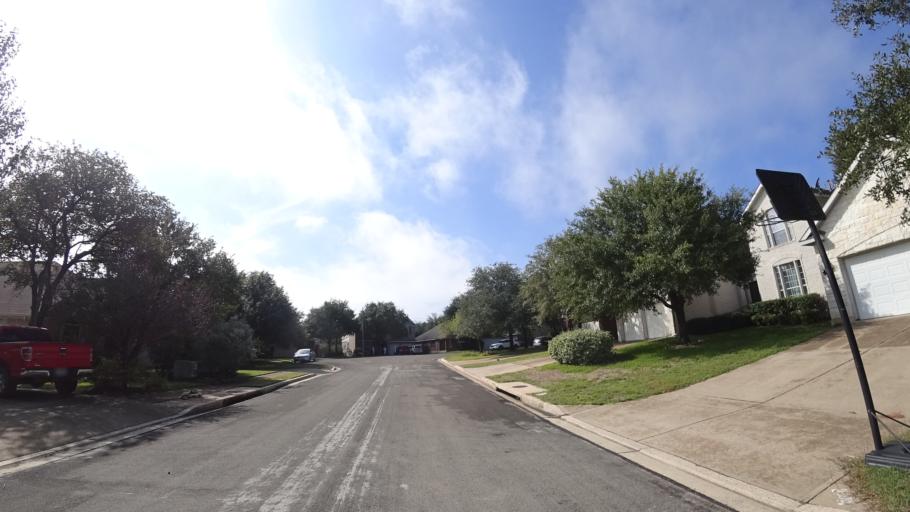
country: US
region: Texas
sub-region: Travis County
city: Shady Hollow
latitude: 30.2048
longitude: -97.8743
